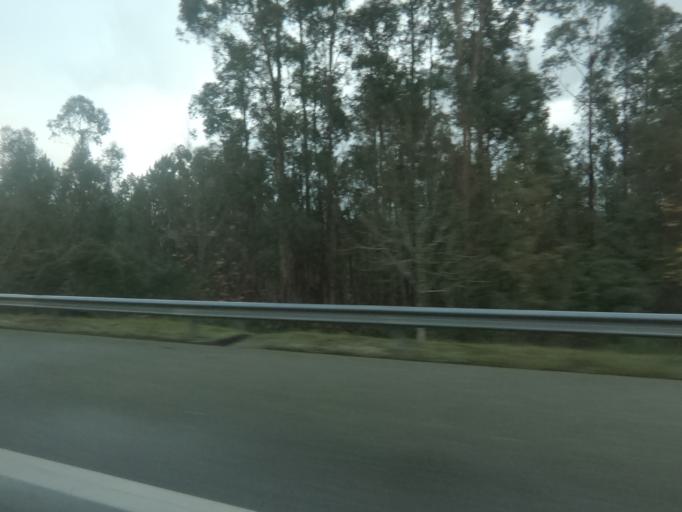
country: PT
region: Braga
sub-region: Barcelos
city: Galegos
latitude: 41.6359
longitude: -8.5607
